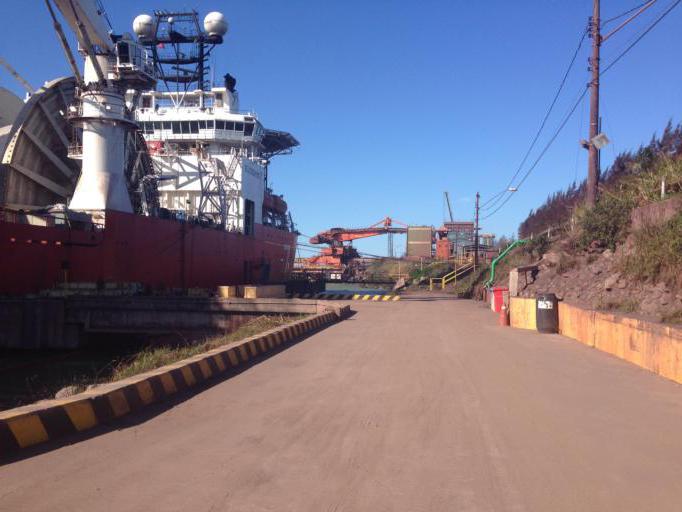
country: BR
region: Espirito Santo
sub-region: Guarapari
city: Guarapari
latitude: -20.7880
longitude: -40.5740
